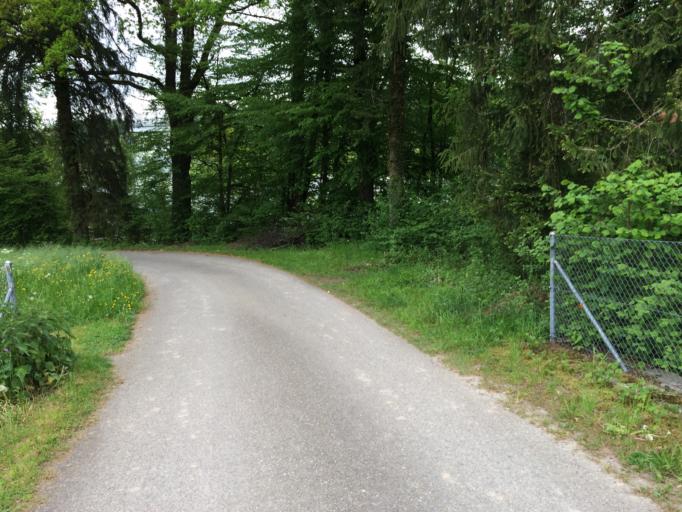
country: CH
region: Zurich
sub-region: Bezirk Uster
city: Uster / Ober-Uster
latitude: 47.3441
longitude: 8.7414
